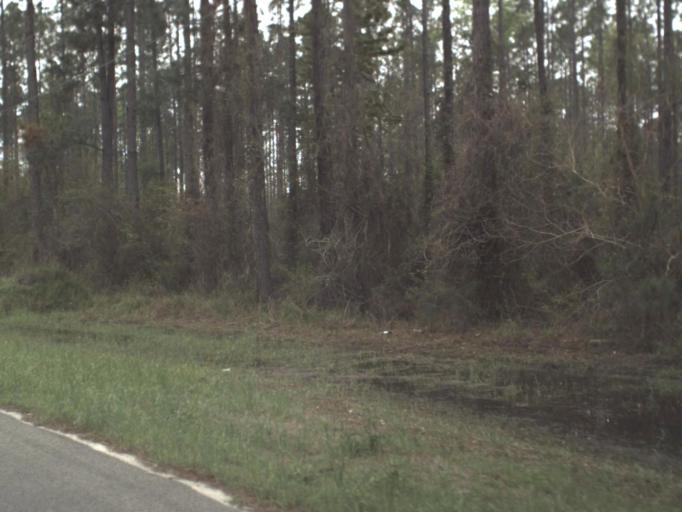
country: US
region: Florida
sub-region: Gulf County
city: Wewahitchka
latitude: 30.0791
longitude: -85.1942
